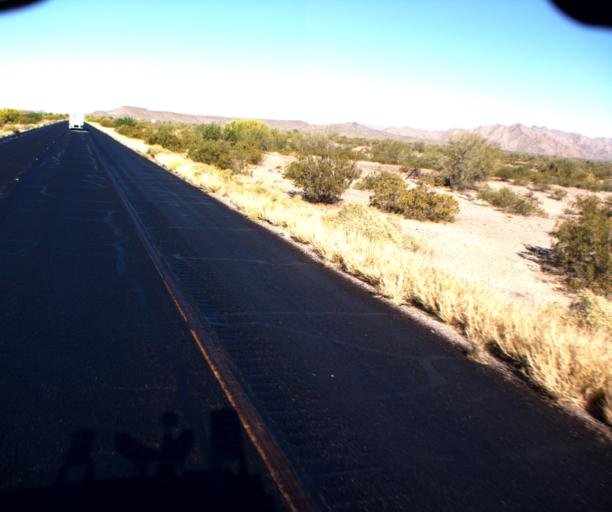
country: US
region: Arizona
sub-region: Pinal County
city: Maricopa
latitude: 32.8447
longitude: -112.2758
